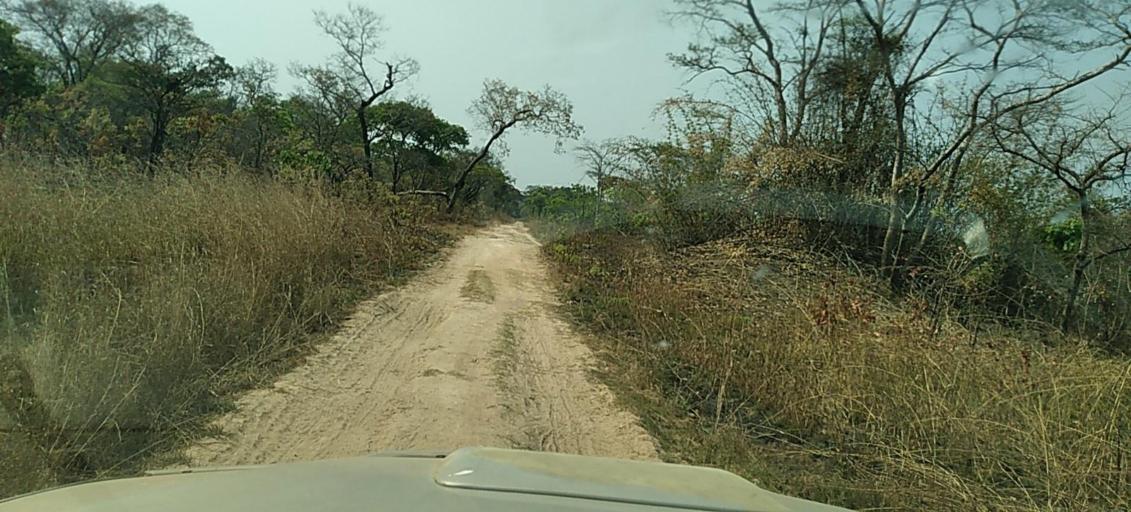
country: ZM
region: North-Western
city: Kasempa
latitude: -13.5405
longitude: 26.4088
